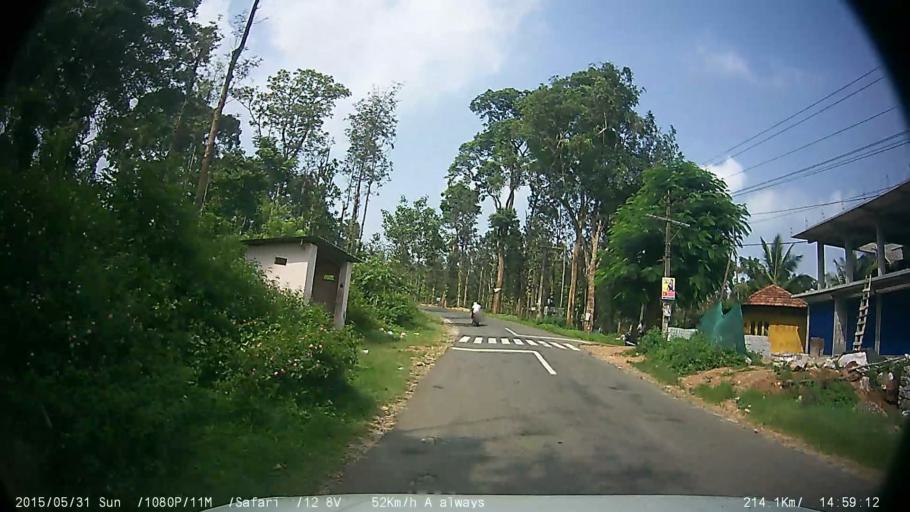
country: IN
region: Kerala
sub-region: Wayanad
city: Kalpetta
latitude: 11.6090
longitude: 76.2091
